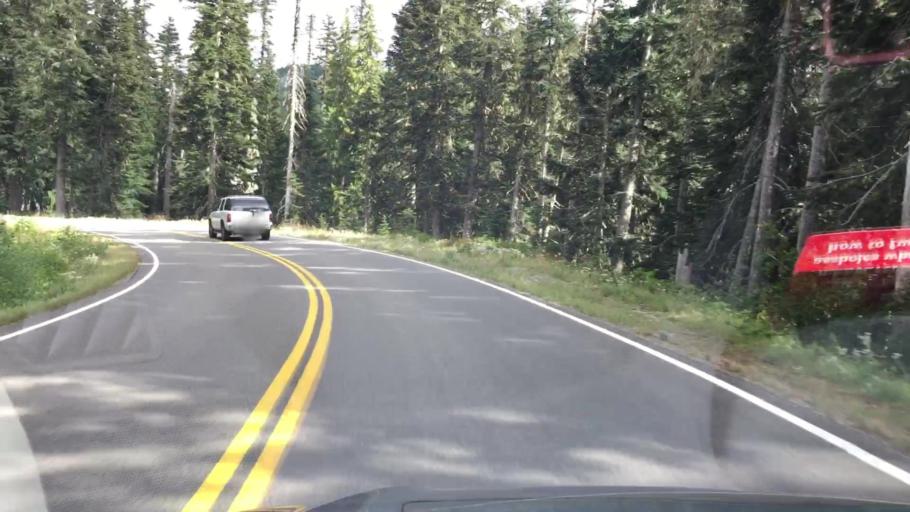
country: US
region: Washington
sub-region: Pierce County
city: Buckley
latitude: 46.7694
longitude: -121.7428
